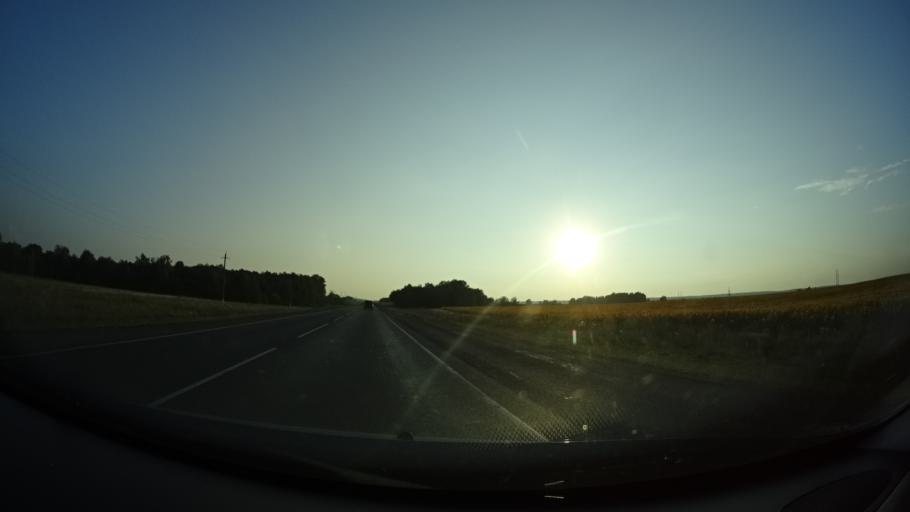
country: RU
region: Samara
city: Isakly
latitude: 54.0151
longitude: 51.7413
